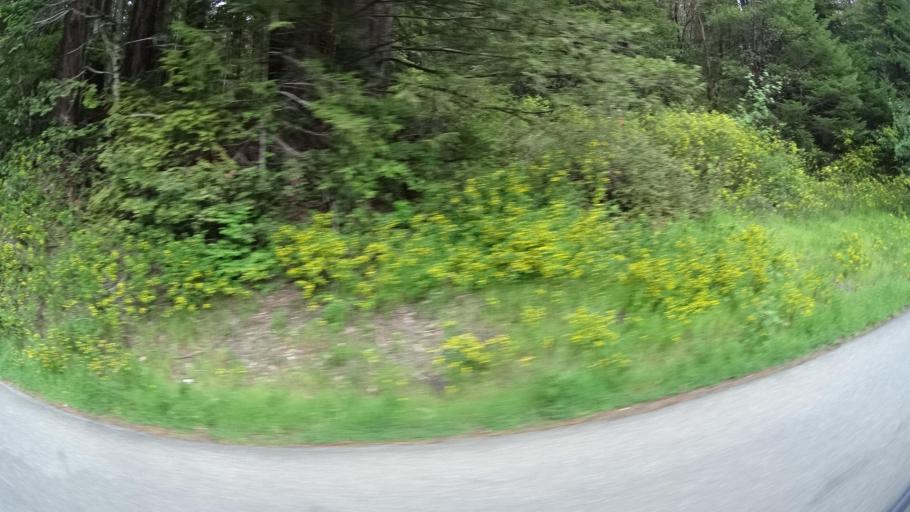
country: US
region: California
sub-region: Humboldt County
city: Redway
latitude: 40.2832
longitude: -123.8439
